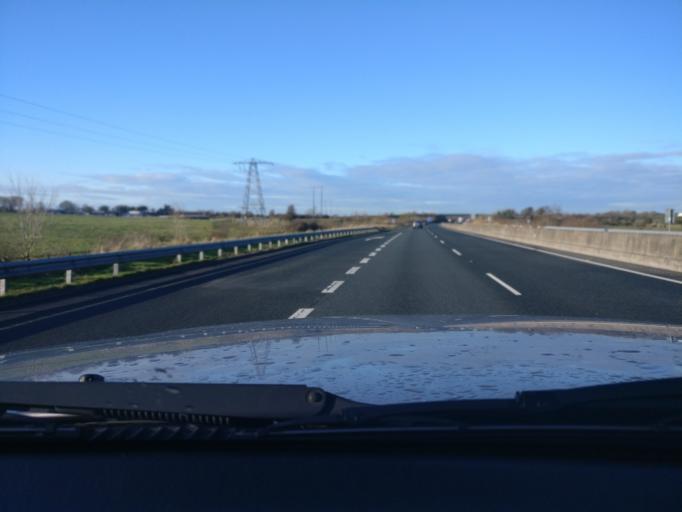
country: IE
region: Connaught
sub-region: County Galway
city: Loughrea
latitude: 53.2646
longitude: -8.6189
